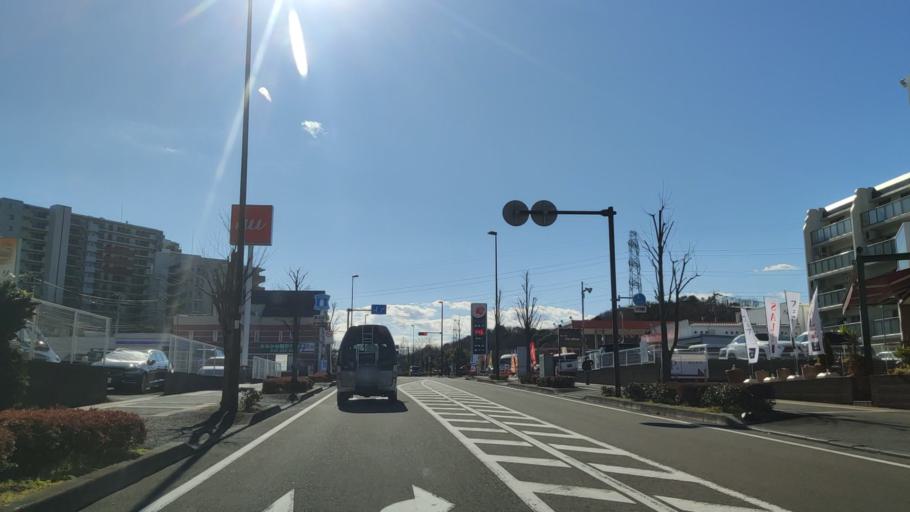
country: JP
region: Tokyo
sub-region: Machida-shi
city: Machida
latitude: 35.5209
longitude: 139.4977
